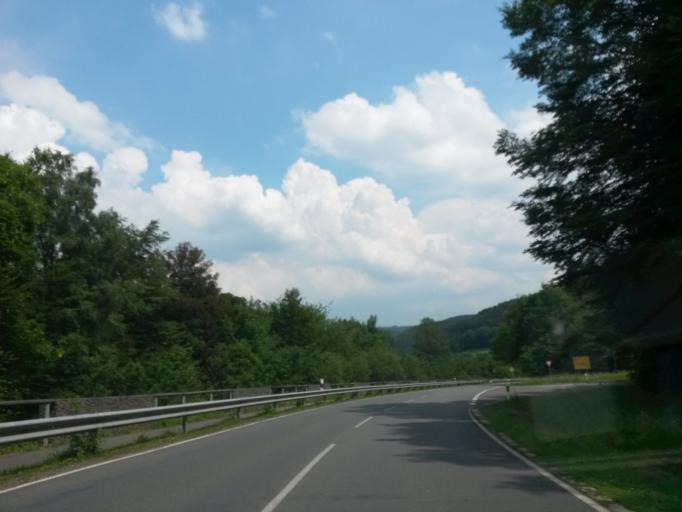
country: DE
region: North Rhine-Westphalia
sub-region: Regierungsbezirk Arnsberg
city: Olpe
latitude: 51.0807
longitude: 7.8611
